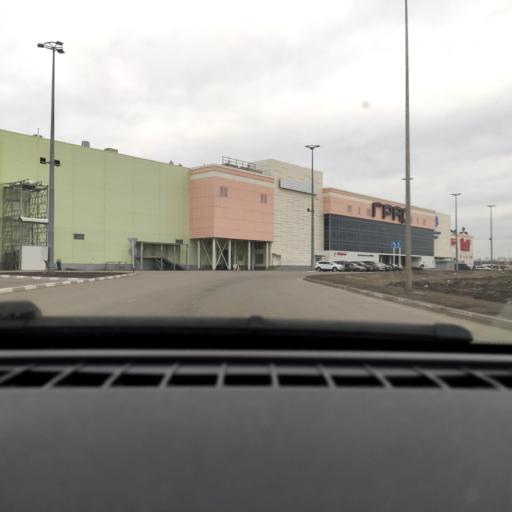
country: RU
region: Voronezj
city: Podgornoye
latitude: 51.7918
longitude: 39.2081
